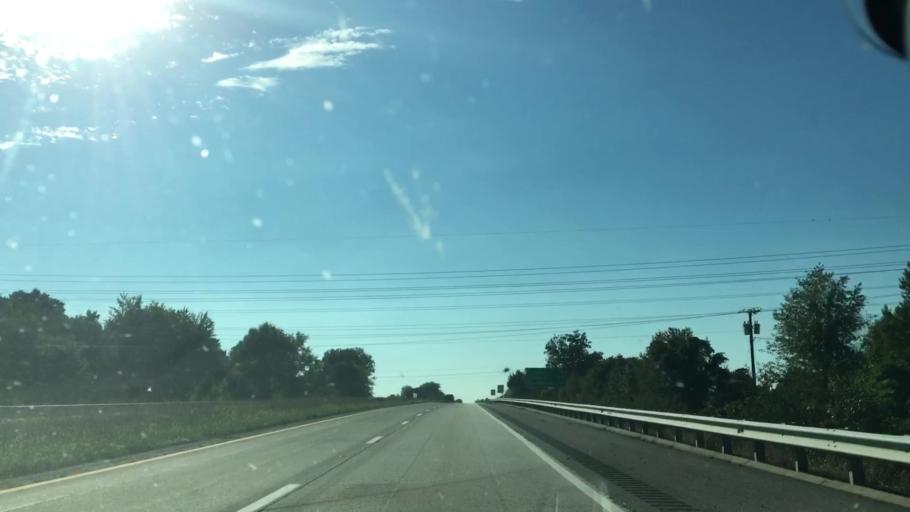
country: US
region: Kentucky
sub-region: Daviess County
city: Owensboro
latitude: 37.7666
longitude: -87.1741
